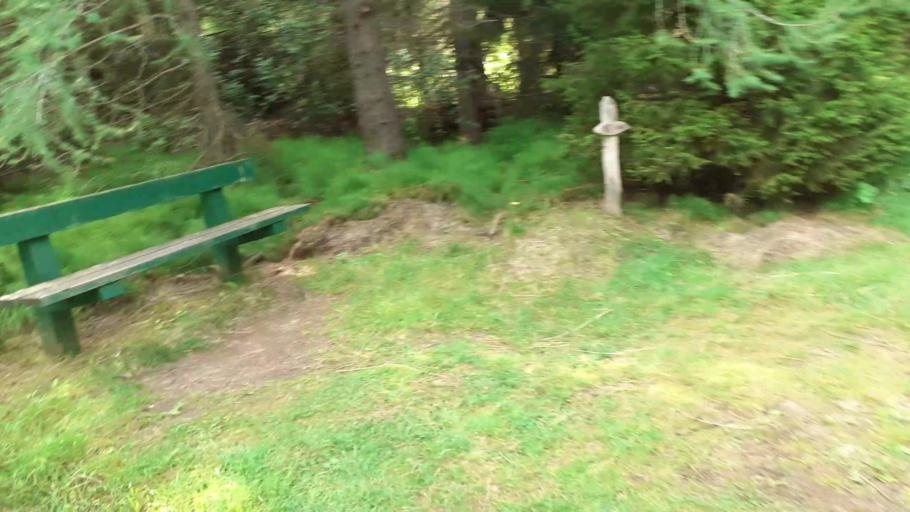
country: IS
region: Northeast
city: Akureyri
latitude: 65.6406
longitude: -18.0950
